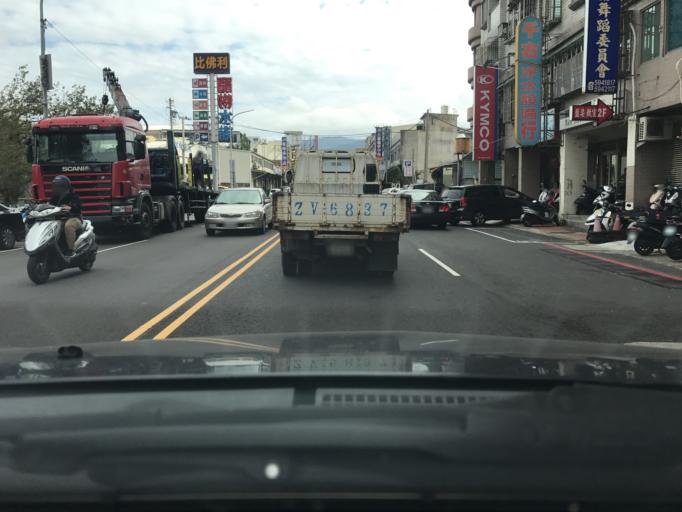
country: TW
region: Taiwan
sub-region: Hsinchu
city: Zhubei
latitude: 24.7356
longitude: 121.0965
